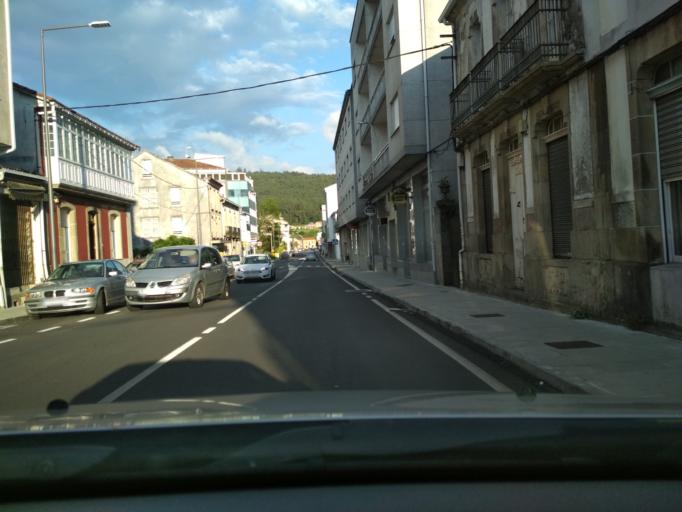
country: ES
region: Galicia
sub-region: Provincia da Coruna
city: Outes
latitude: 42.8429
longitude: -8.9074
